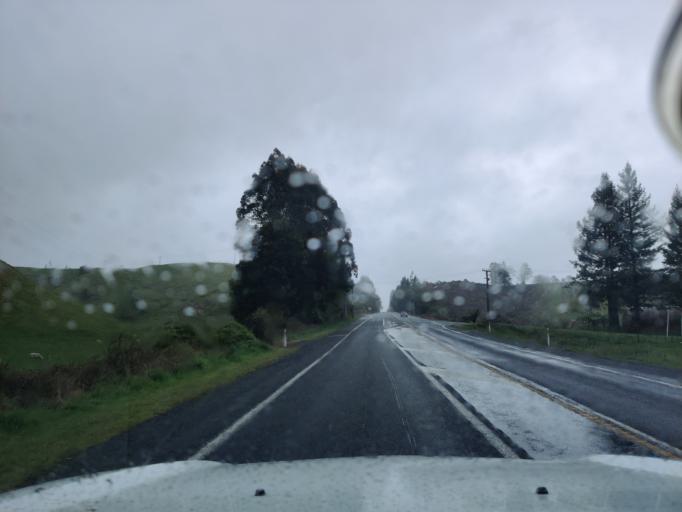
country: NZ
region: Bay of Plenty
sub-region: Rotorua District
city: Rotorua
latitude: -38.0841
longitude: 176.1886
